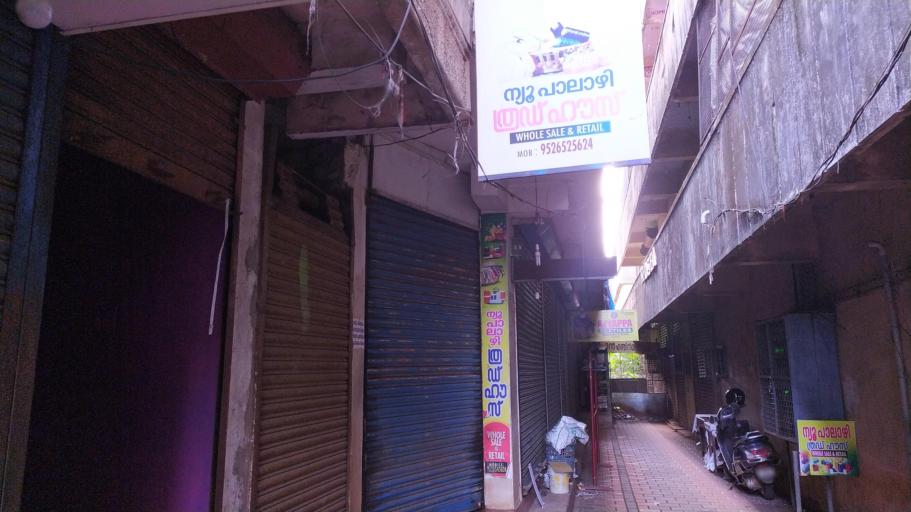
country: IN
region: Kerala
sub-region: Kasaragod District
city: Kannangad
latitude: 12.3228
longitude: 75.0863
